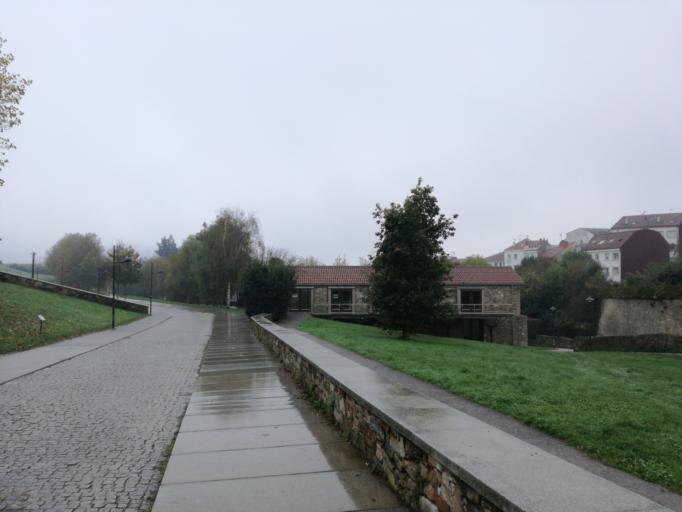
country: ES
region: Galicia
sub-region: Provincia da Coruna
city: Santiago de Compostela
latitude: 42.8785
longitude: -8.5387
